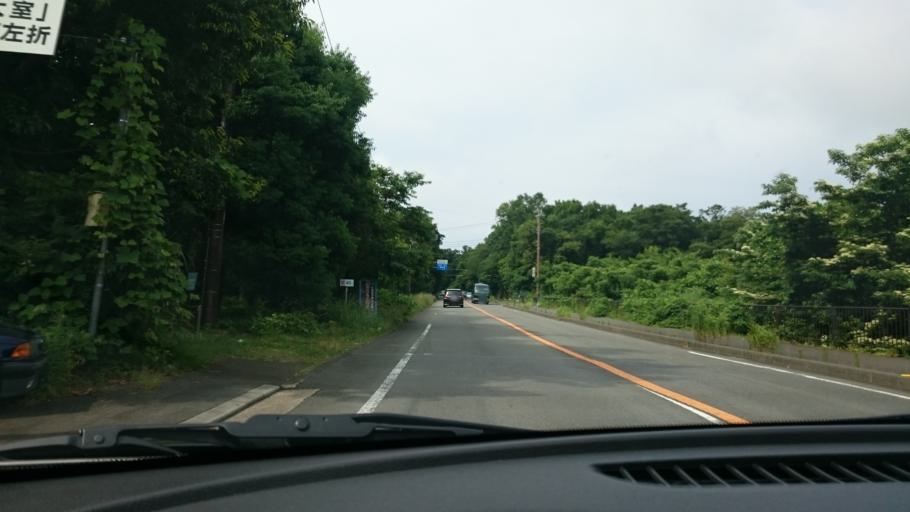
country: JP
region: Shizuoka
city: Ito
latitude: 34.8978
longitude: 139.1208
